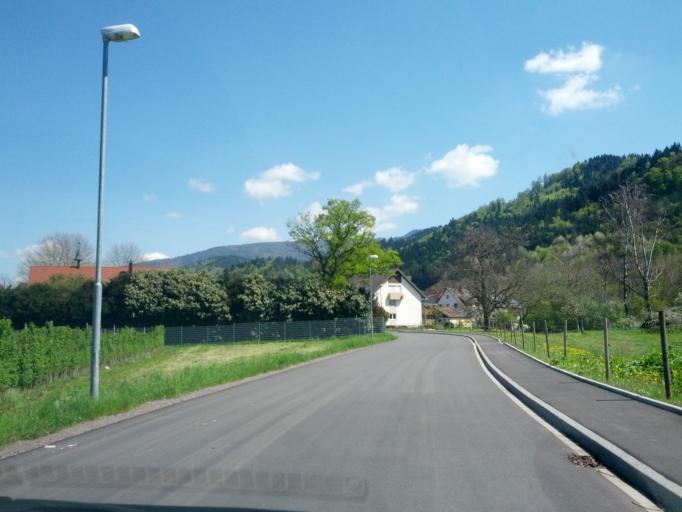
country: DE
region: Baden-Wuerttemberg
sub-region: Freiburg Region
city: Sexau
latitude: 48.0800
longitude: 7.9238
